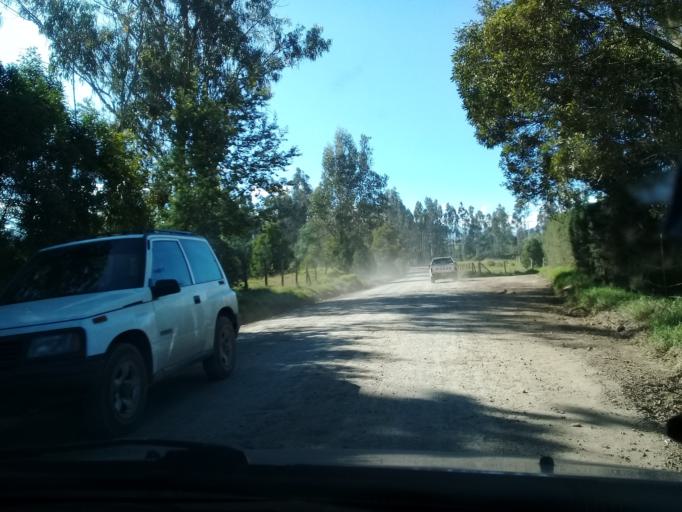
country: CO
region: Cundinamarca
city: Guasca
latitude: 4.8963
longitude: -73.8831
